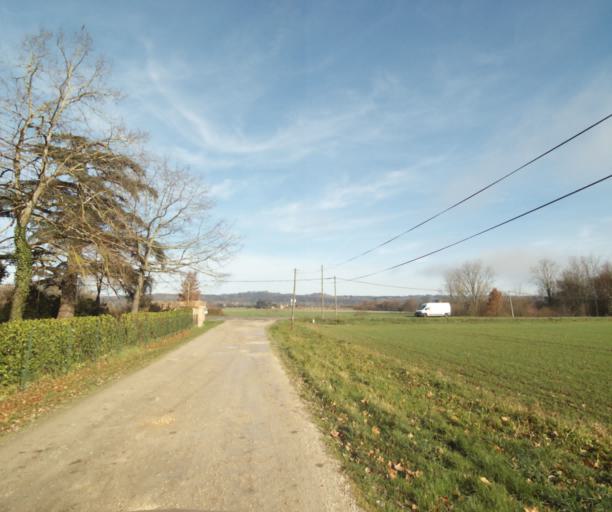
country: FR
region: Midi-Pyrenees
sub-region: Departement de la Haute-Garonne
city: Villemur-sur-Tarn
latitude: 43.8629
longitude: 1.4775
